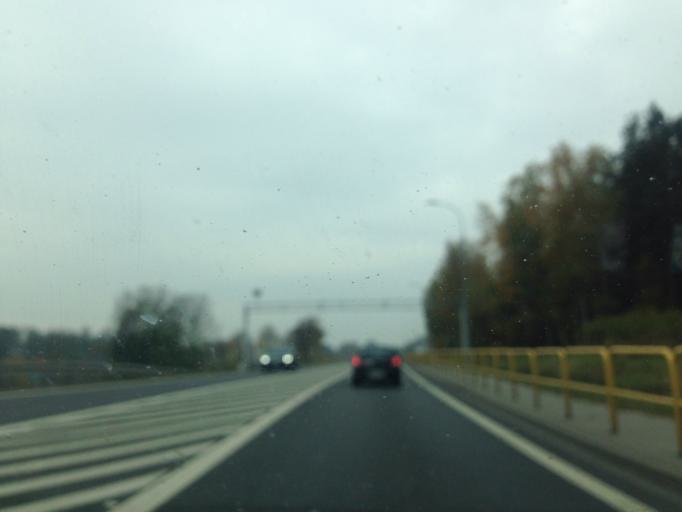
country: PL
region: Kujawsko-Pomorskie
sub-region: Grudziadz
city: Grudziadz
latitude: 53.4935
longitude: 18.6787
